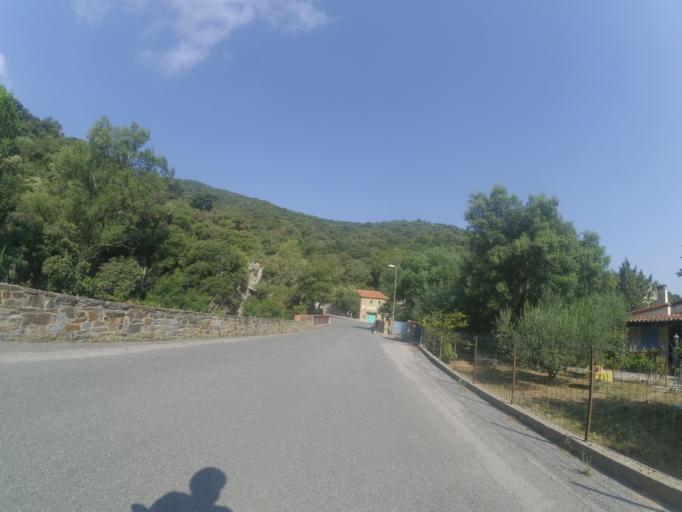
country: FR
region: Languedoc-Roussillon
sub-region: Departement des Pyrenees-Orientales
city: Ille-sur-Tet
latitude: 42.6452
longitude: 2.6246
